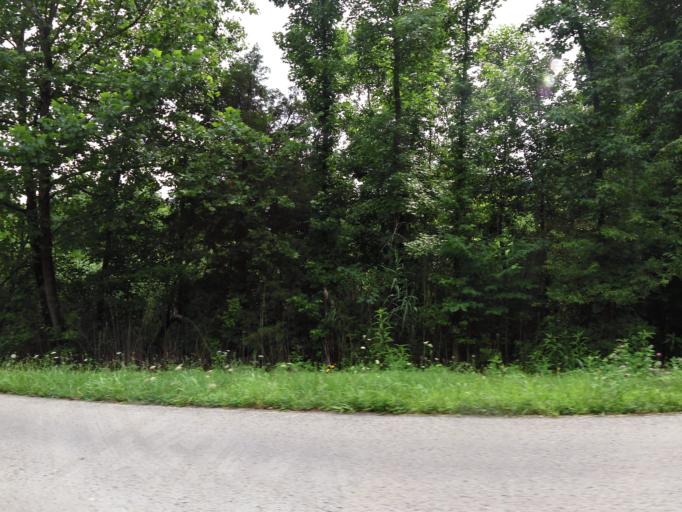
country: US
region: Kentucky
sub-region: Muhlenberg County
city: Morehead
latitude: 37.3023
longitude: -87.3209
